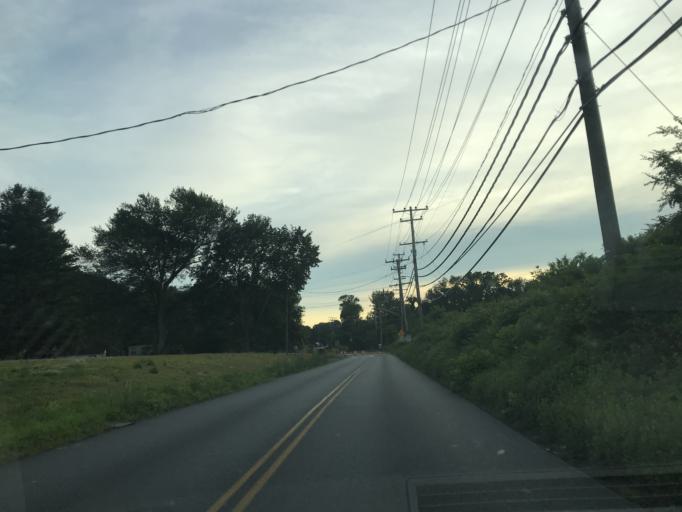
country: US
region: Maryland
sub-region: Harford County
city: Perryman
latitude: 39.4883
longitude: -76.1894
